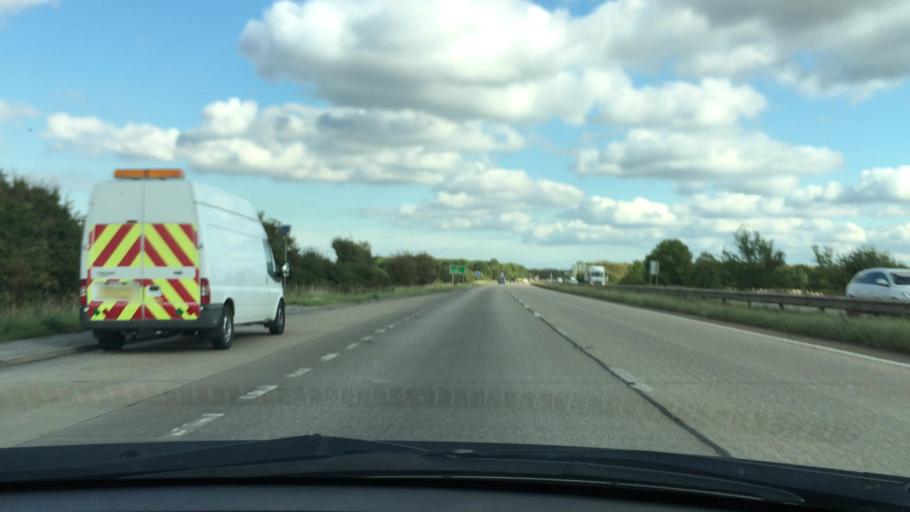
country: GB
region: England
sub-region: North East Lincolnshire
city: Healing
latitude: 53.5956
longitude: -0.1816
